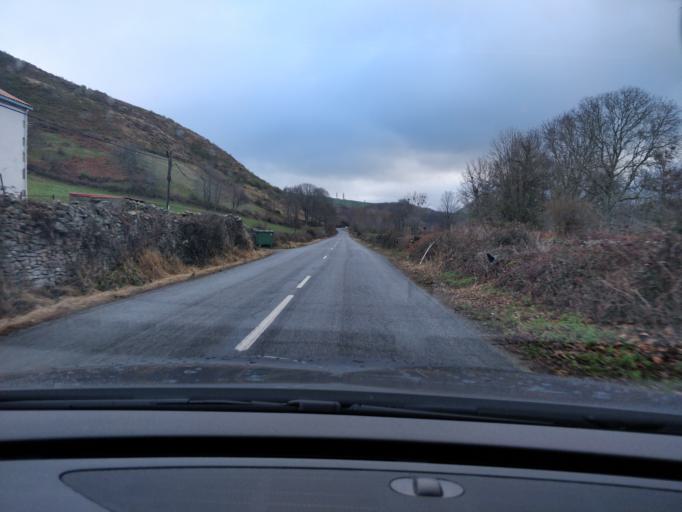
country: ES
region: Castille and Leon
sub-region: Provincia de Burgos
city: Espinosa de los Monteros
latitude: 43.0929
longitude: -3.5613
